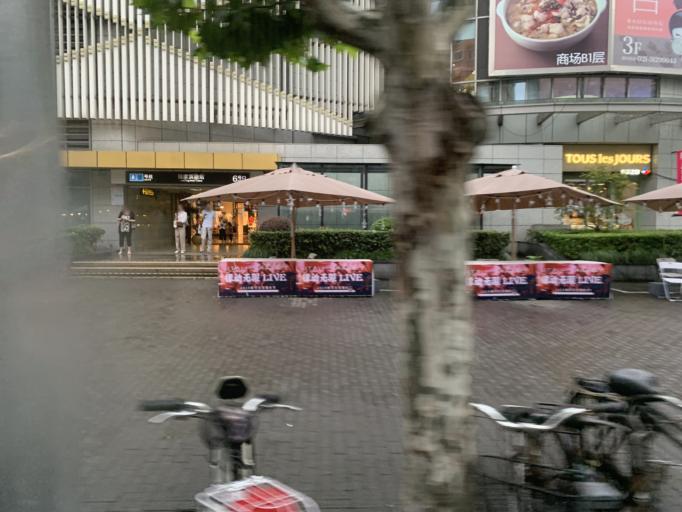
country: CN
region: Shanghai Shi
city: Luwan
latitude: 31.2137
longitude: 121.4822
